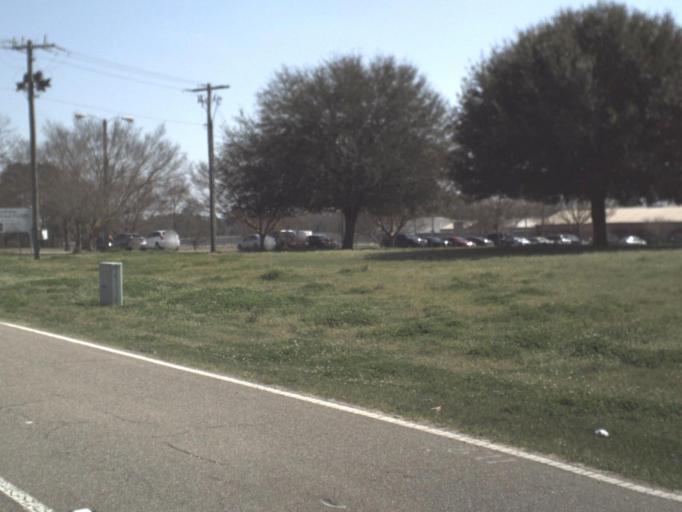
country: US
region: Florida
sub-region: Gadsden County
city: Gretna
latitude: 30.5922
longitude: -84.6567
